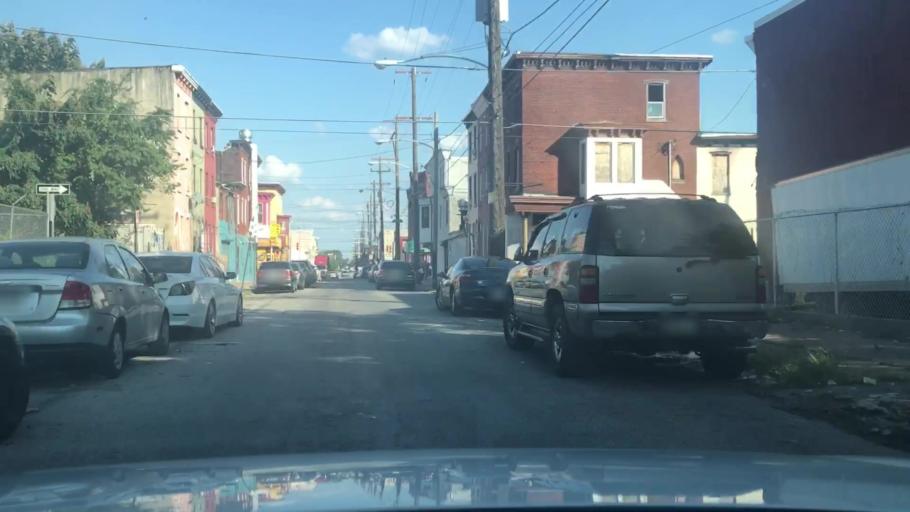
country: US
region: Pennsylvania
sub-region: Philadelphia County
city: Philadelphia
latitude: 39.9892
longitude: -75.1419
